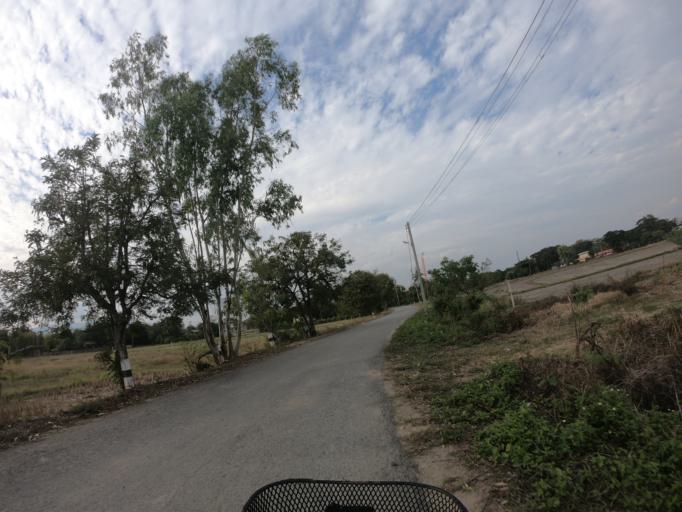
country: TH
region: Chiang Mai
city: San Sai
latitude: 18.7981
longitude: 99.0526
